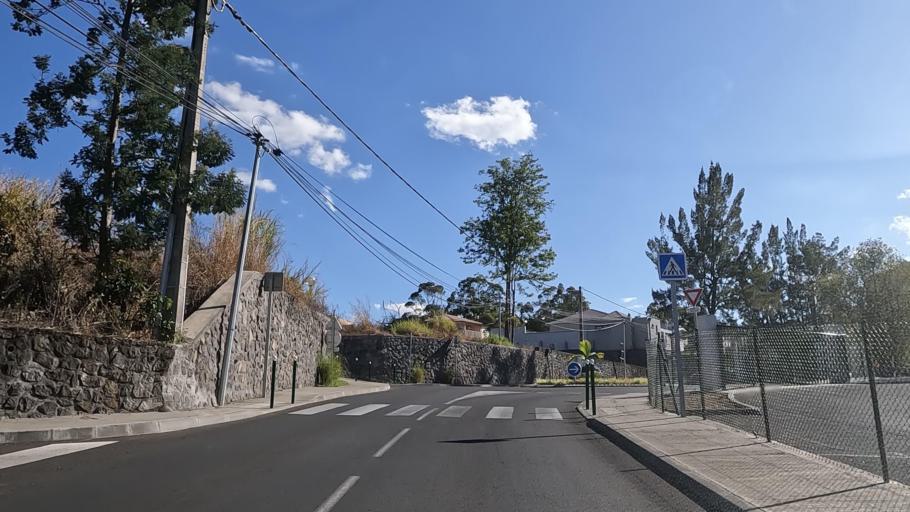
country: RE
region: Reunion
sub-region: Reunion
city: Le Tampon
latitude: -21.2593
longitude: 55.5104
